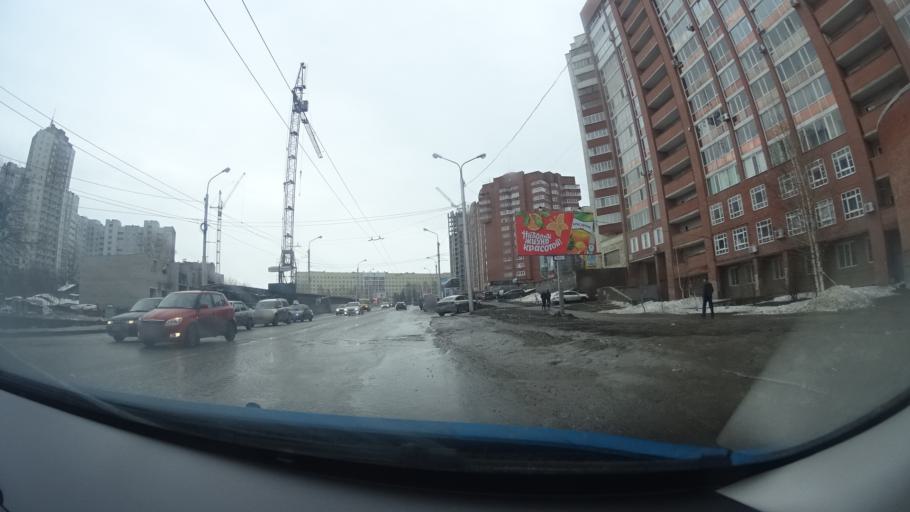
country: RU
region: Bashkortostan
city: Ufa
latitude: 54.7131
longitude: 55.9968
